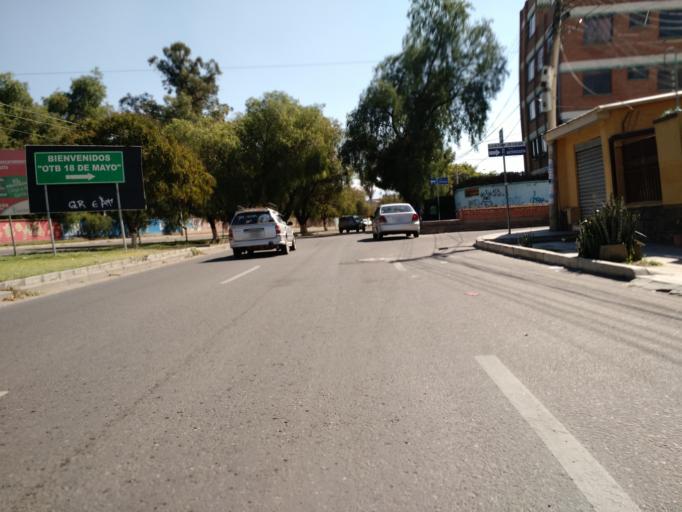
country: BO
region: Cochabamba
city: Cochabamba
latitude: -17.3877
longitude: -66.1808
